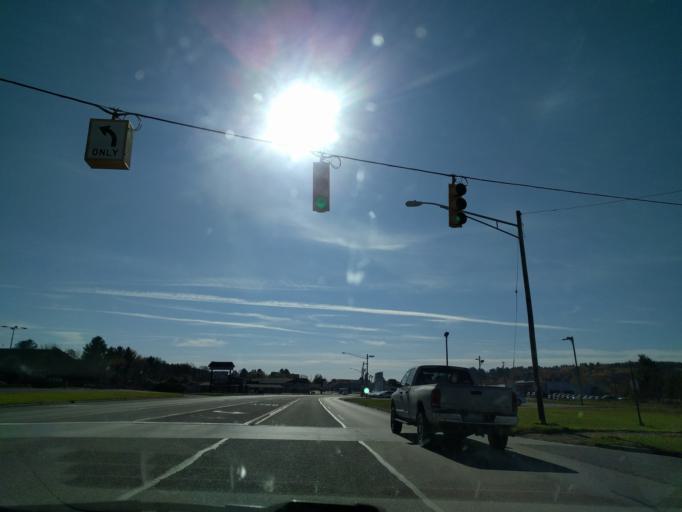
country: US
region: Michigan
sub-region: Dickinson County
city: Iron Mountain
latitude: 45.8401
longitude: -88.0509
